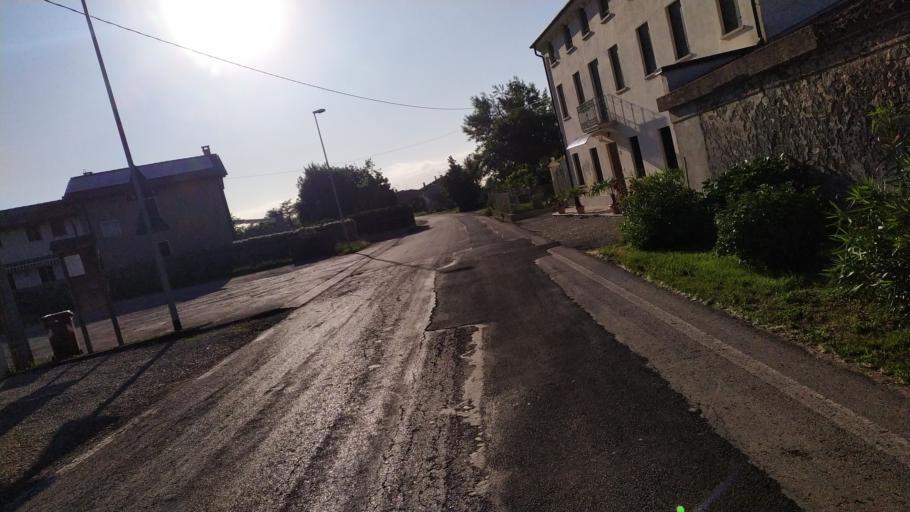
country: IT
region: Veneto
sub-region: Provincia di Vicenza
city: Isola Vicentina
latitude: 45.6330
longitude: 11.4262
